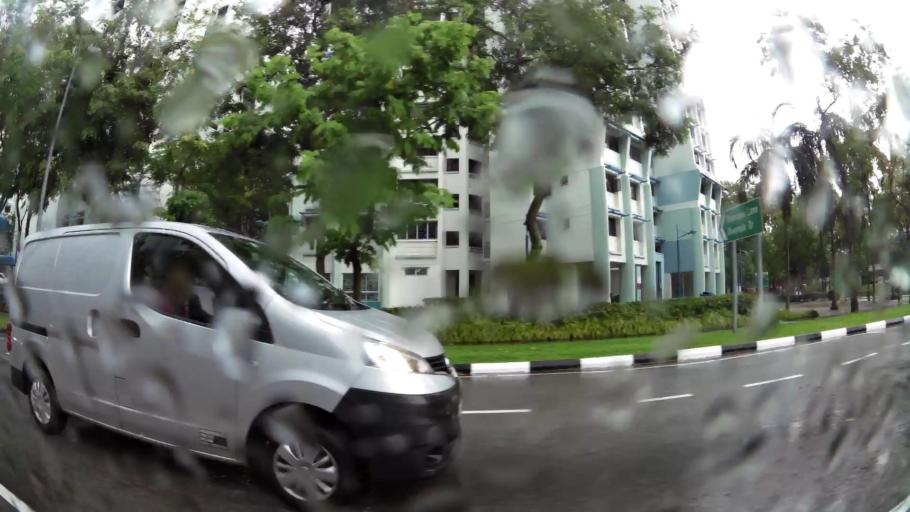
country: MY
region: Johor
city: Kampung Pasir Gudang Baru
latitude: 1.3866
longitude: 103.9018
